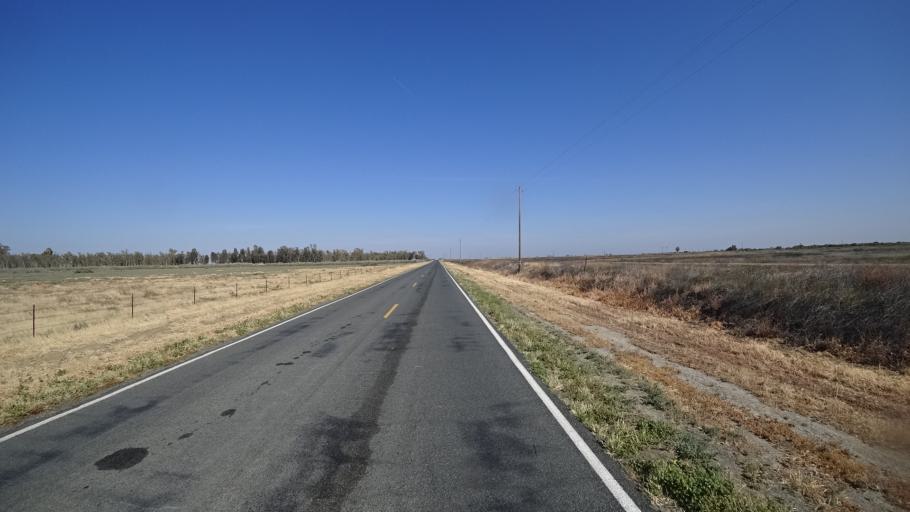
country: US
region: California
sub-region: Fresno County
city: Riverdale
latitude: 36.3745
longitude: -119.9267
